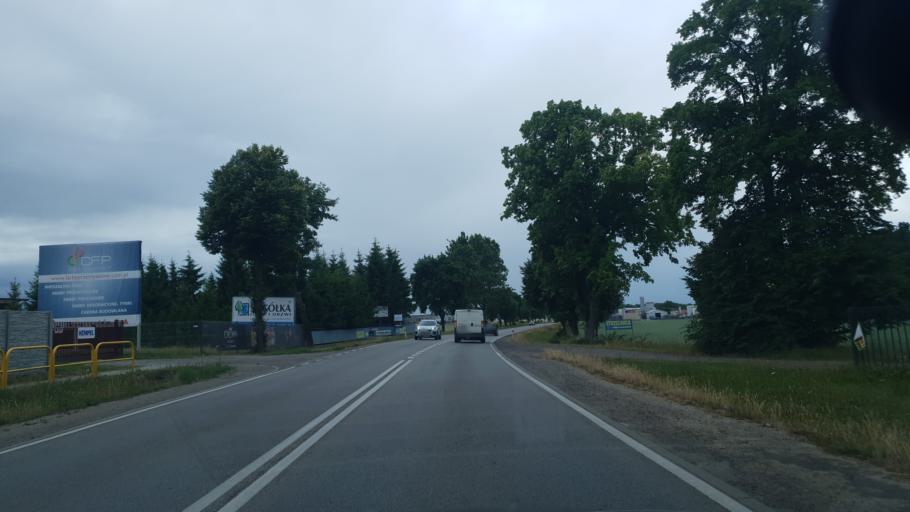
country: PL
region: Pomeranian Voivodeship
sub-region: Powiat kartuski
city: Banino
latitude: 54.4096
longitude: 18.3697
